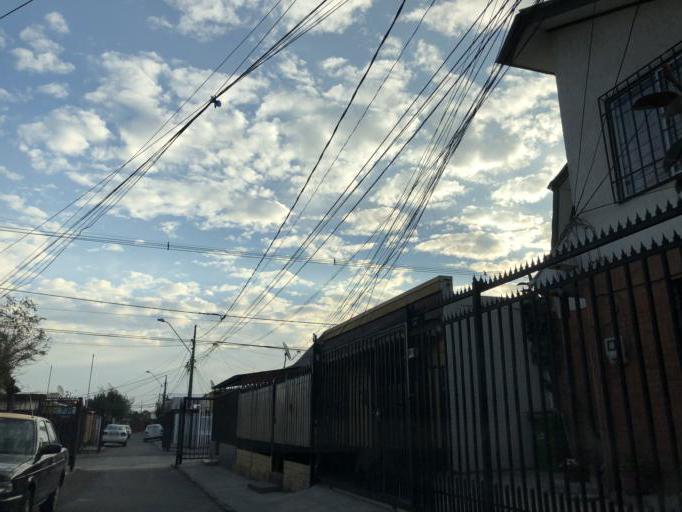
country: CL
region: Santiago Metropolitan
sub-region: Provincia de Cordillera
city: Puente Alto
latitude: -33.6176
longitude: -70.5801
